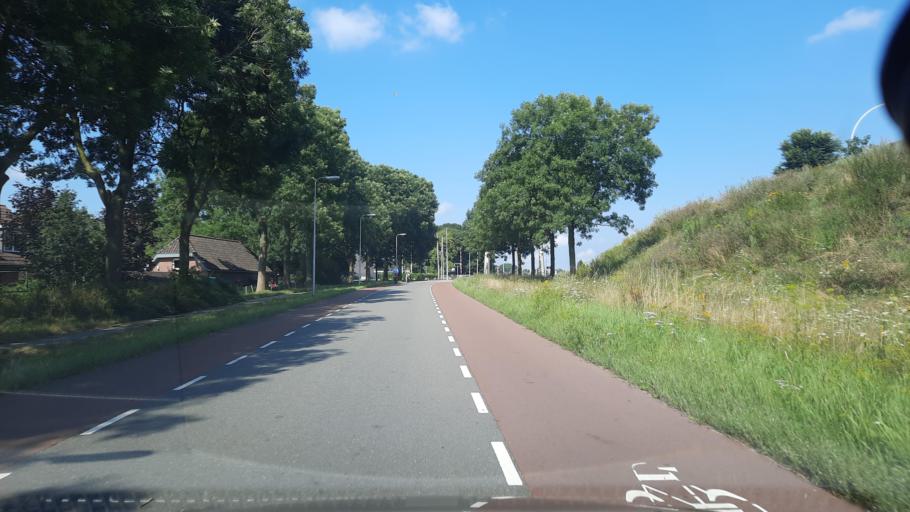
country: NL
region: Gelderland
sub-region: Gemeente Hattem
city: Hattem
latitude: 52.5092
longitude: 6.0567
